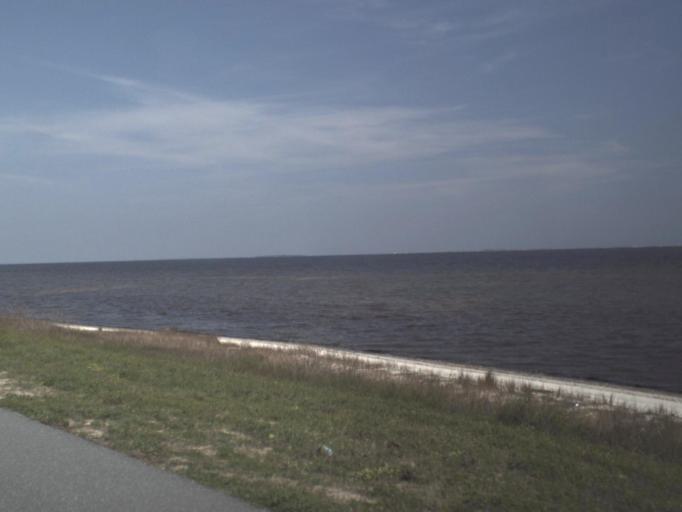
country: US
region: Florida
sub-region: Franklin County
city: Eastpoint
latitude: 29.7704
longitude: -84.7967
